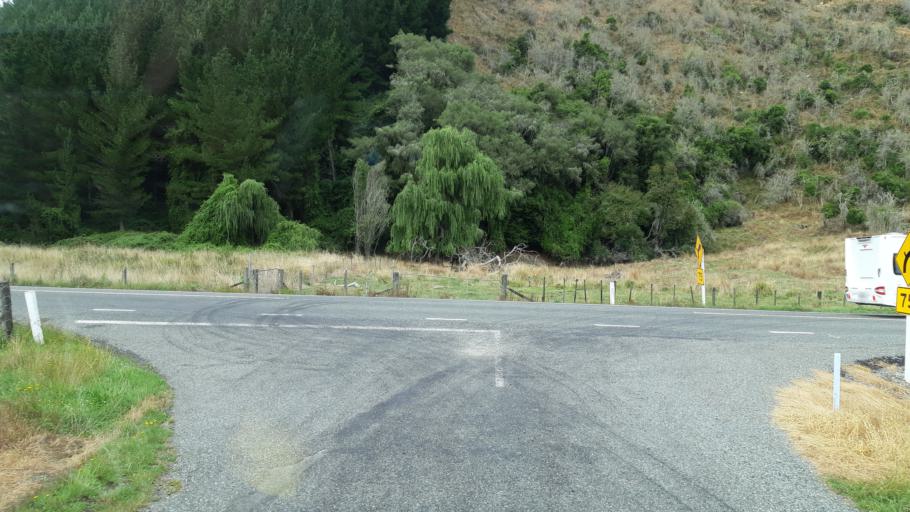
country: NZ
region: West Coast
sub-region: Buller District
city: Westport
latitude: -41.7945
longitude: 172.2957
